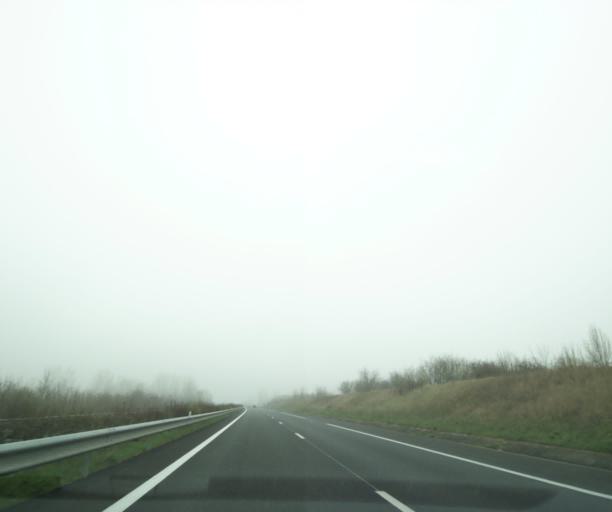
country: FR
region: Midi-Pyrenees
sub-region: Departement du Tarn-et-Garonne
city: Realville
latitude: 44.1119
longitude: 1.4675
